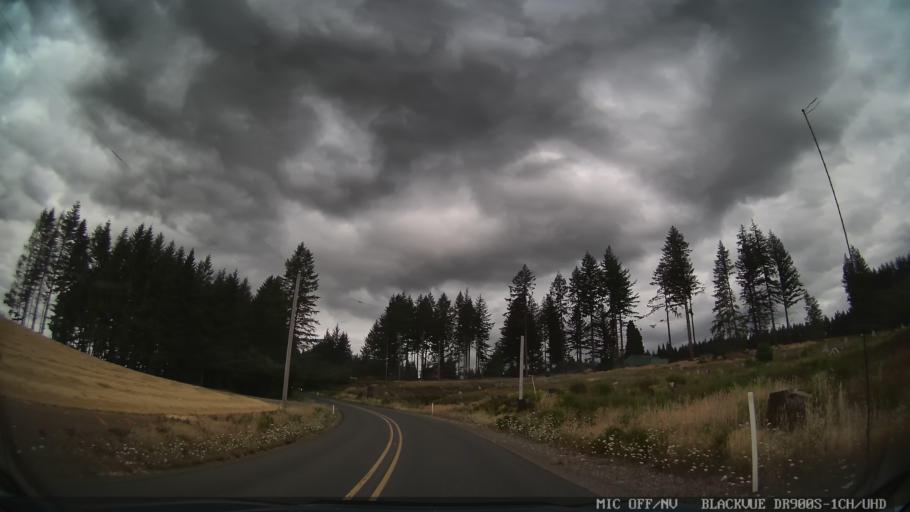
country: US
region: Oregon
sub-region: Linn County
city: Lyons
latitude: 44.8495
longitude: -122.6648
